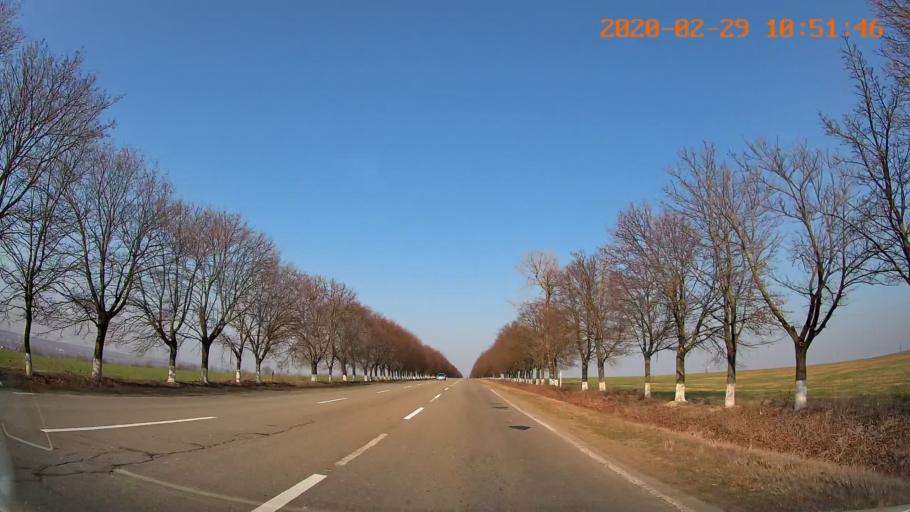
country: MD
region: Telenesti
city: Grigoriopol
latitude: 47.0969
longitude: 29.3598
